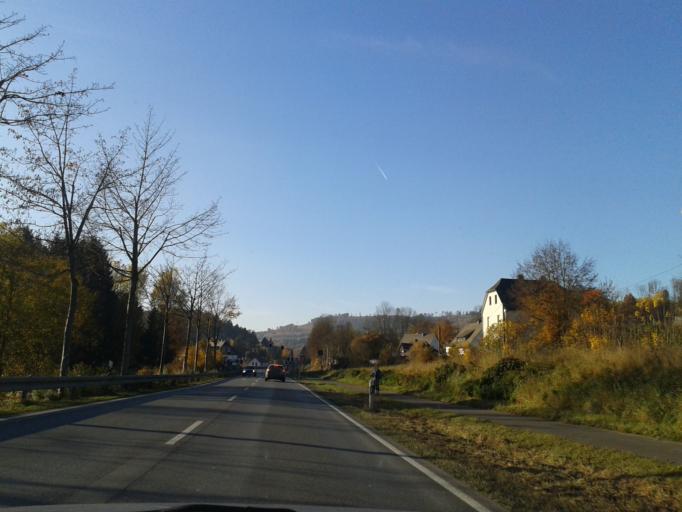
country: DE
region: North Rhine-Westphalia
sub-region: Regierungsbezirk Arnsberg
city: Bestwig
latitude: 51.3649
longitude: 8.4394
